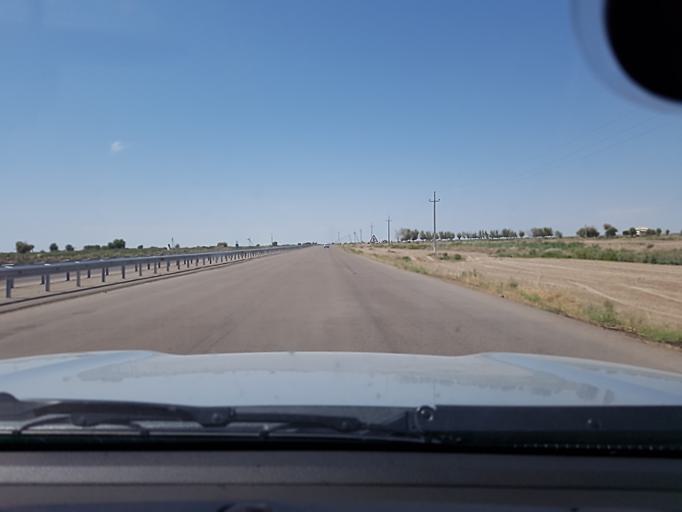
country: TM
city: Akdepe
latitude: 41.7367
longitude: 59.1198
